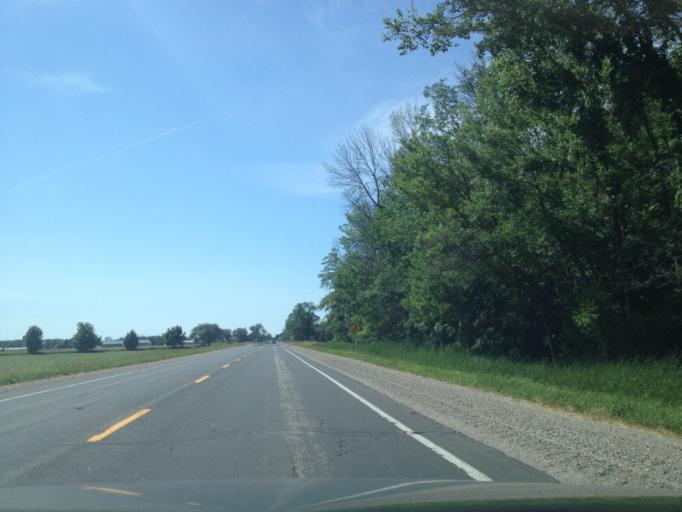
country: CA
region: Ontario
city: Stratford
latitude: 43.4952
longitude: -80.8621
